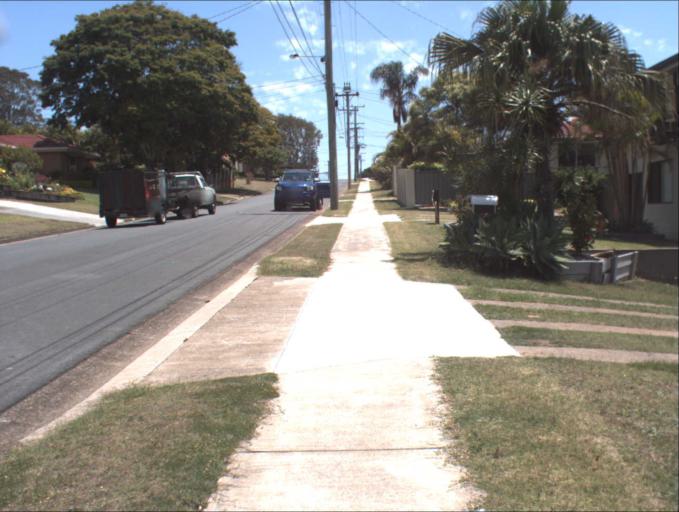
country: AU
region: Queensland
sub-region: Logan
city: Rochedale South
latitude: -27.5923
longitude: 153.1405
